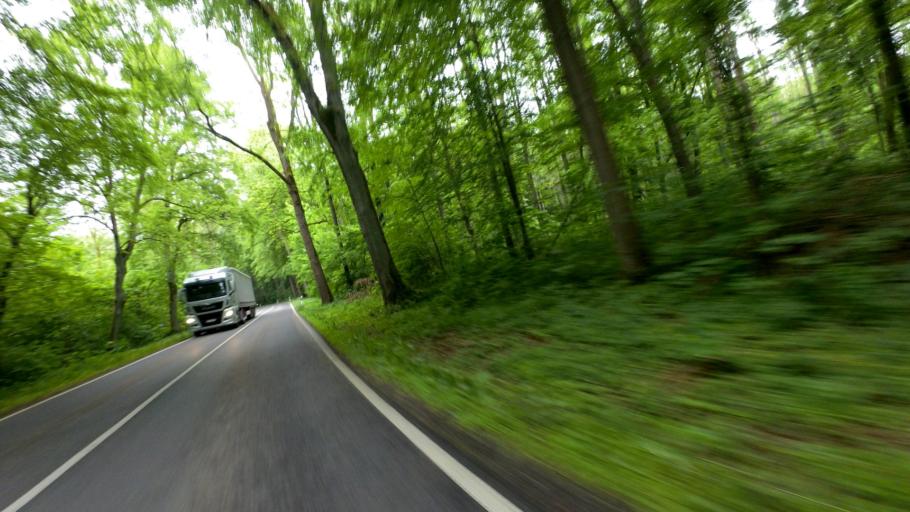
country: DE
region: Brandenburg
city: Templin
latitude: 53.0677
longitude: 13.5147
